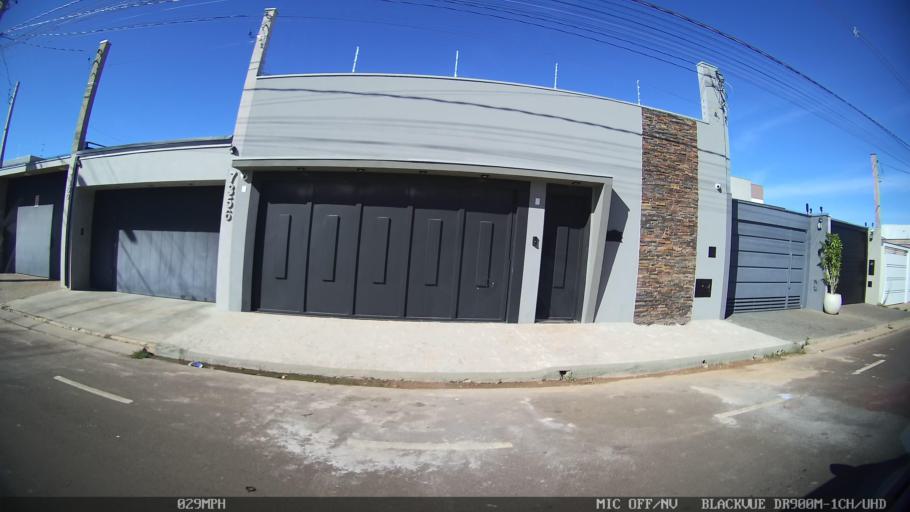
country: BR
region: Sao Paulo
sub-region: Franca
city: Franca
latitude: -20.5688
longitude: -47.3506
